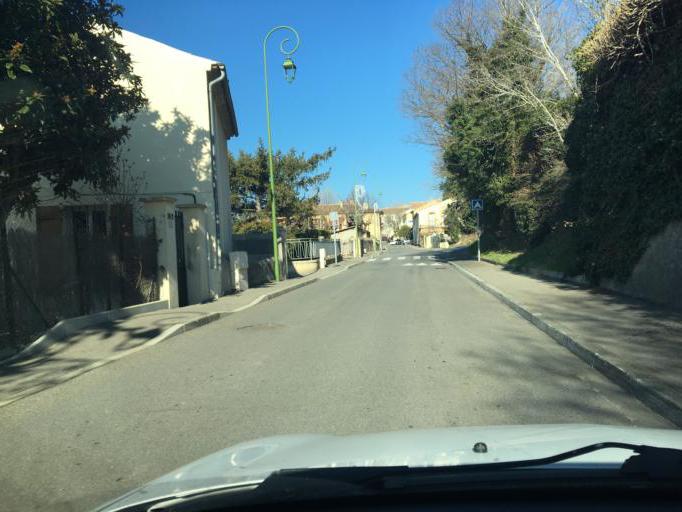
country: FR
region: Provence-Alpes-Cote d'Azur
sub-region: Departement des Bouches-du-Rhone
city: Mallemort
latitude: 43.7279
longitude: 5.1811
